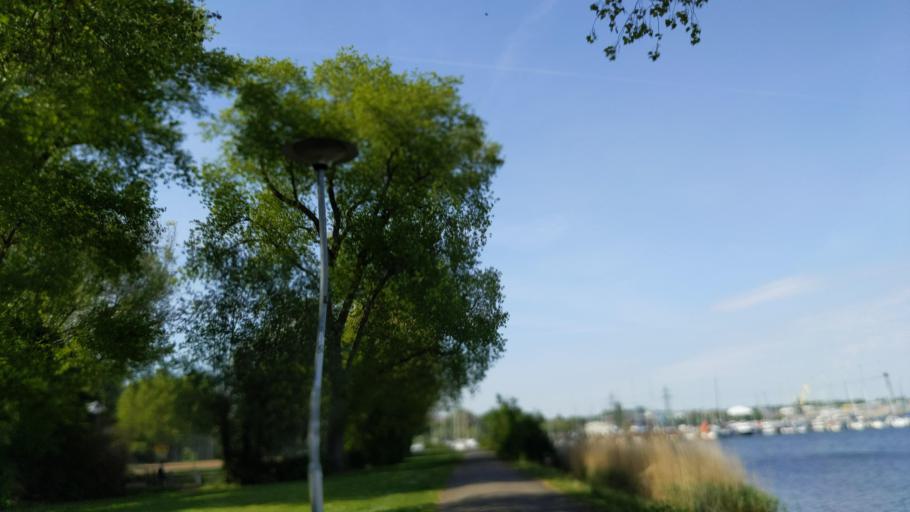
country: DE
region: Mecklenburg-Vorpommern
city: Selmsdorf
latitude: 53.8875
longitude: 10.8031
